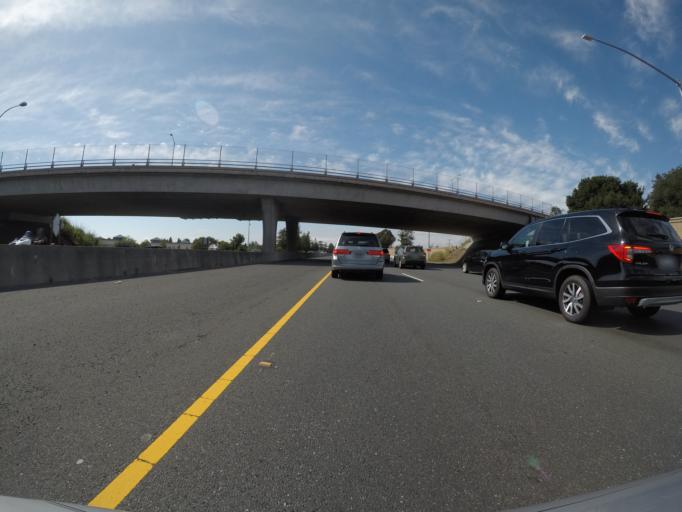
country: US
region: California
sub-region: Sonoma County
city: Petaluma
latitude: 38.2374
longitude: -122.6200
